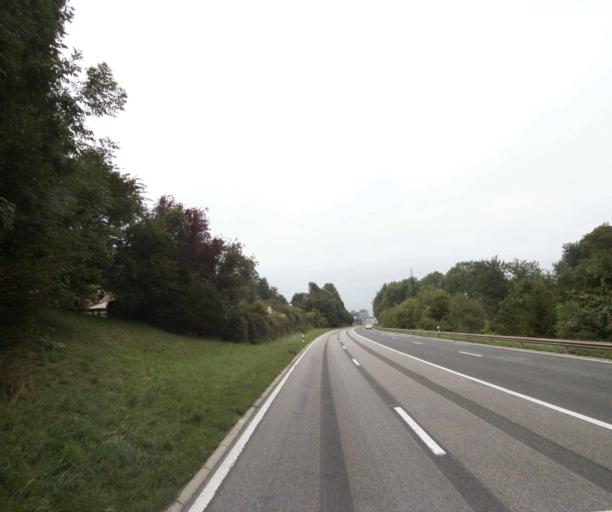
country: CH
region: Vaud
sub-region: Lausanne District
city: Epalinges
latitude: 46.5467
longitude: 6.6644
